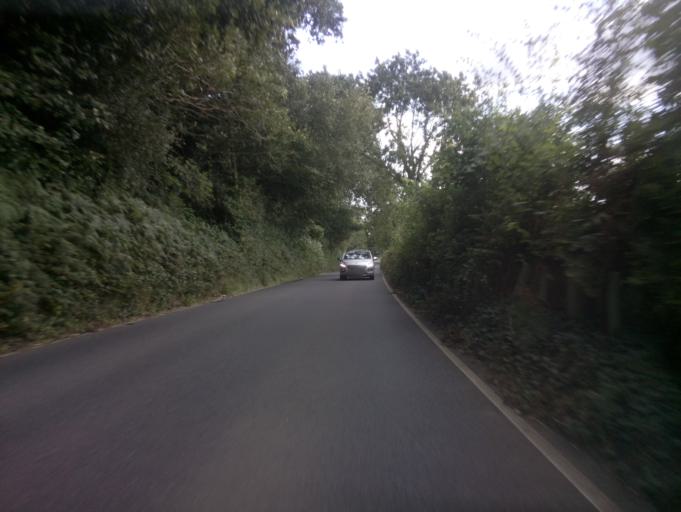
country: GB
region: England
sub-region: Devon
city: Sidmouth
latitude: 50.7398
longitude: -3.2106
